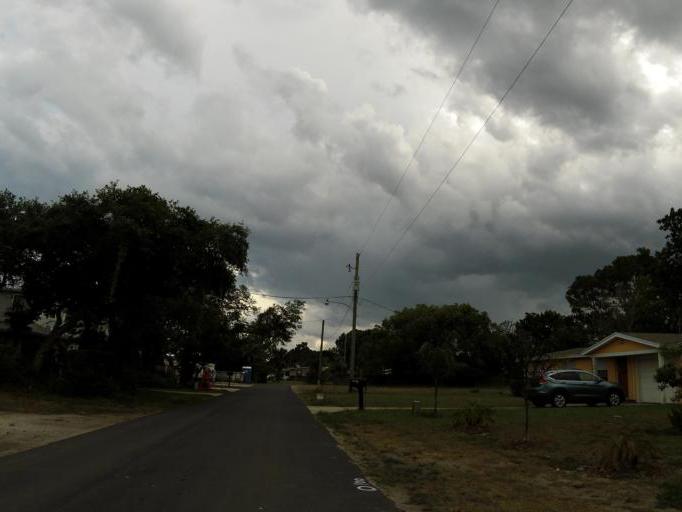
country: US
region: Florida
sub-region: Duval County
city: Jacksonville Beach
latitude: 30.2719
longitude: -81.3930
